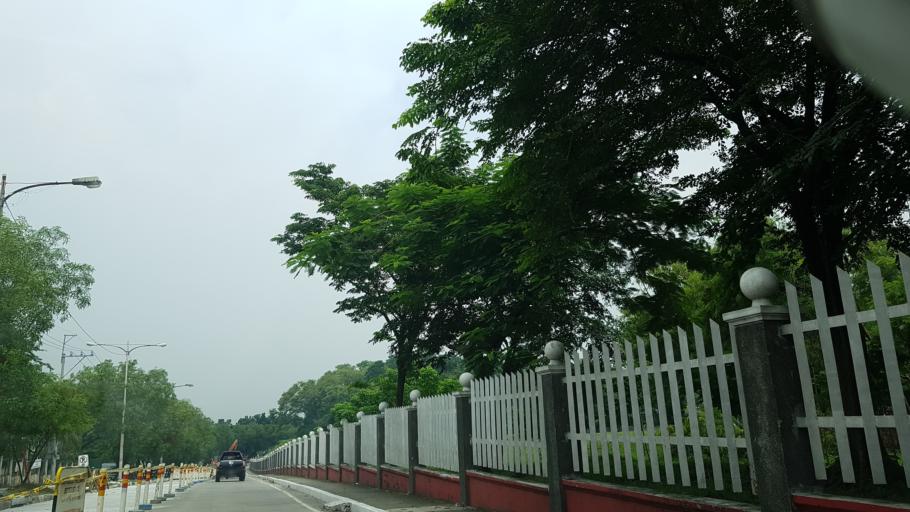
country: PH
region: Metro Manila
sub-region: Makati City
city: Makati City
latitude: 14.5250
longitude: 121.0440
